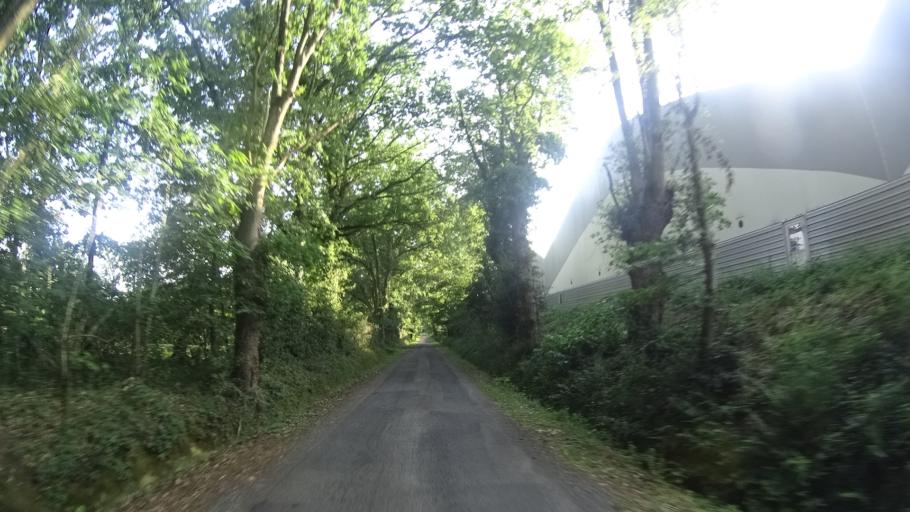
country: FR
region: Brittany
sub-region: Departement d'Ille-et-Vilaine
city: Redon
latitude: 47.6735
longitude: -2.0714
